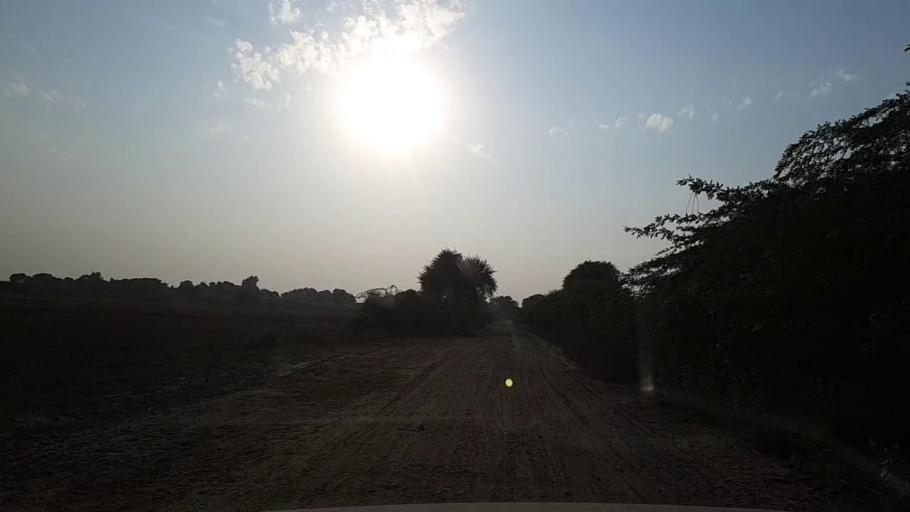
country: PK
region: Sindh
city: Daro Mehar
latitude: 24.7740
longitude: 68.2042
